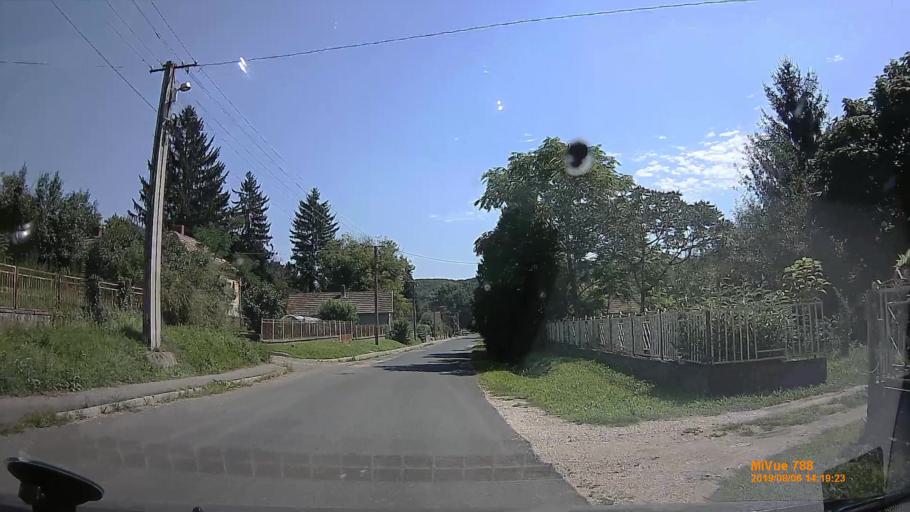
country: HU
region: Zala
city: Zalakomar
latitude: 46.5304
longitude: 17.0884
